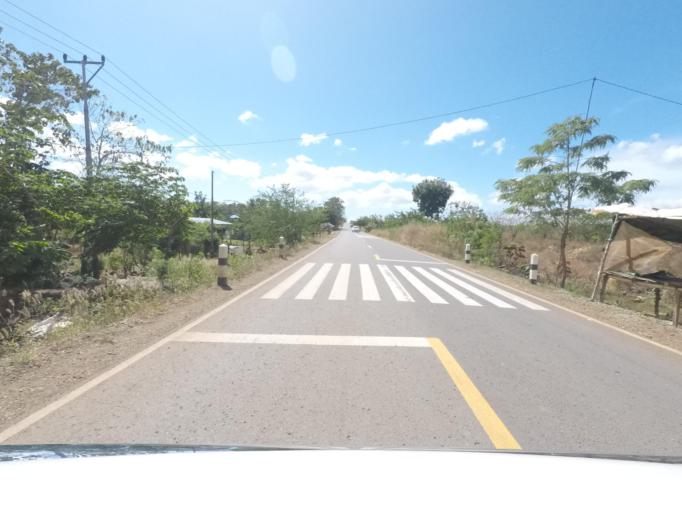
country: TL
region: Baucau
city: Baucau
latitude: -8.4893
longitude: 126.3711
